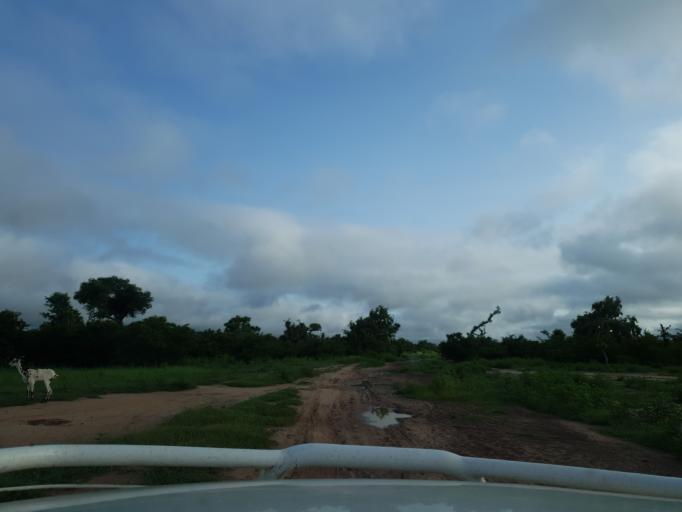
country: ML
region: Segou
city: Baroueli
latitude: 13.3910
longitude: -7.0062
